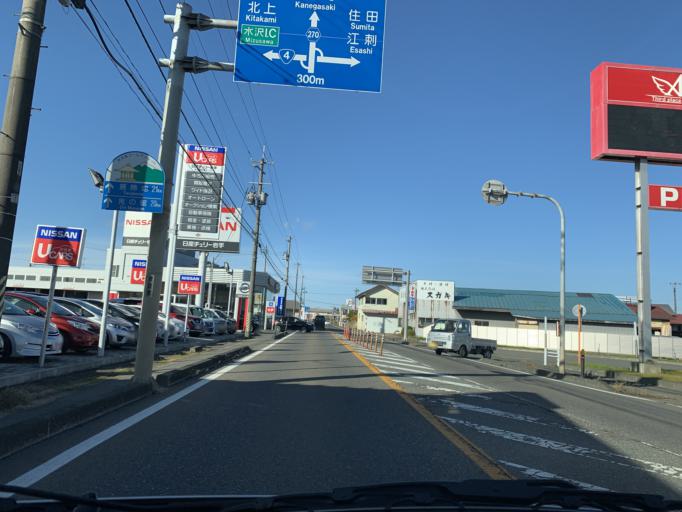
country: JP
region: Iwate
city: Mizusawa
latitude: 39.1658
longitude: 141.1433
